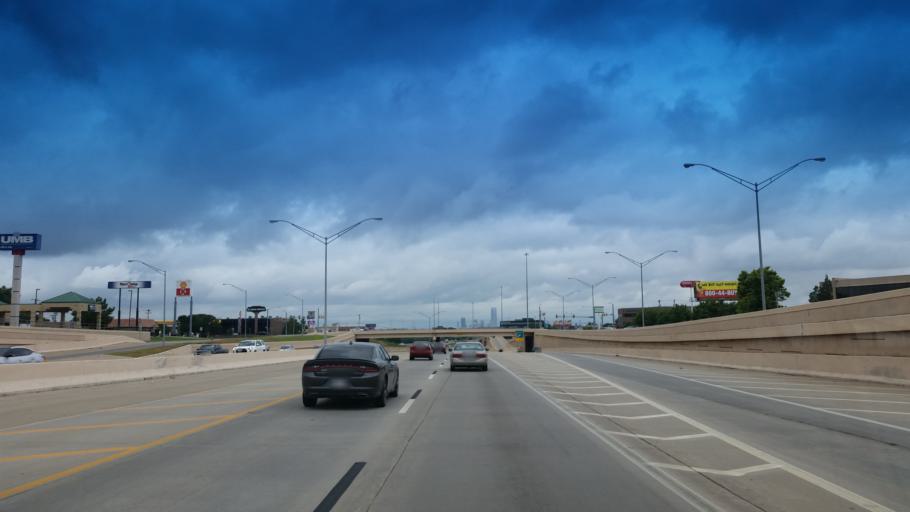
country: US
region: Oklahoma
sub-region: Oklahoma County
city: Nichols Hills
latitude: 35.5395
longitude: -97.5142
